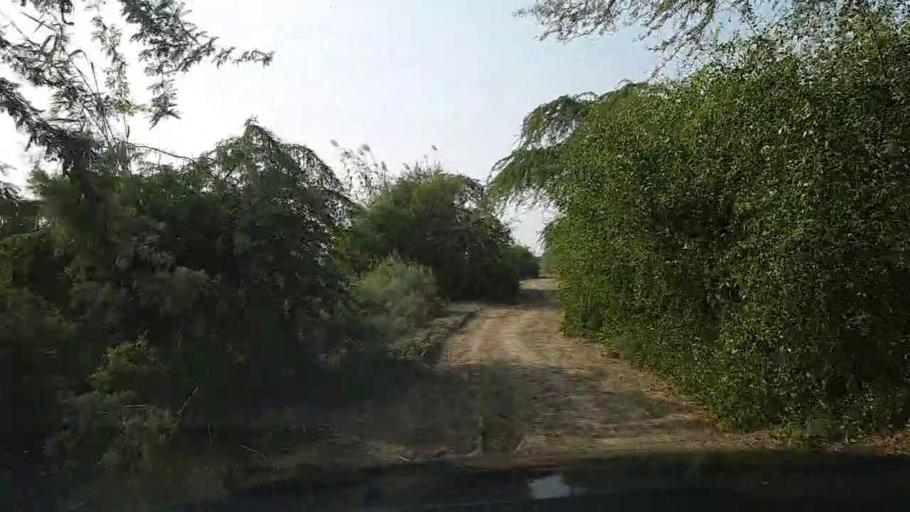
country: PK
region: Sindh
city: Mirpur Batoro
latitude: 24.6485
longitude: 68.2768
